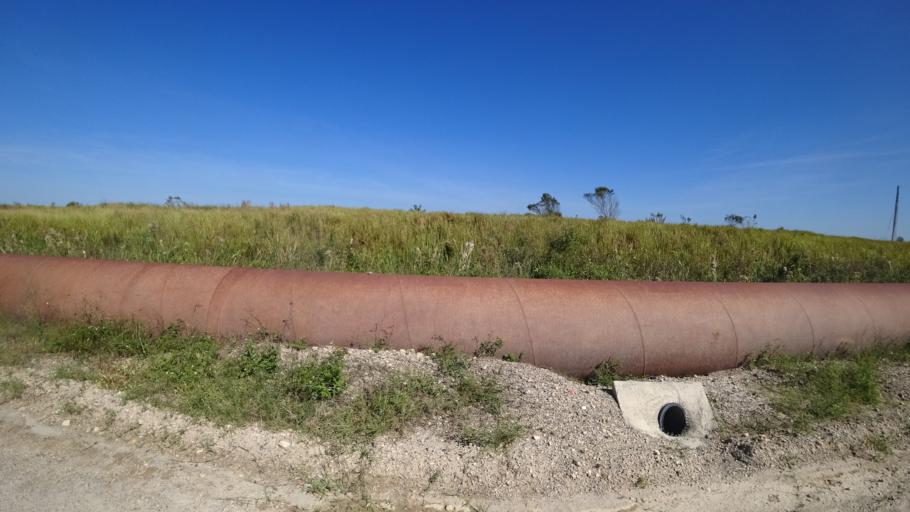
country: US
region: Florida
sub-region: Hillsborough County
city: Balm
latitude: 27.6492
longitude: -82.0839
